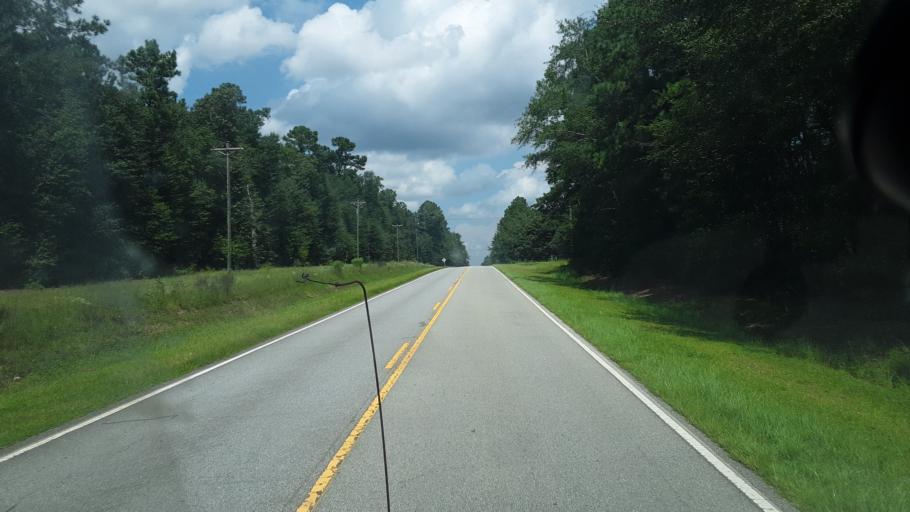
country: US
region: South Carolina
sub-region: Calhoun County
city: Oak Grove
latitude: 33.7473
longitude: -80.9605
